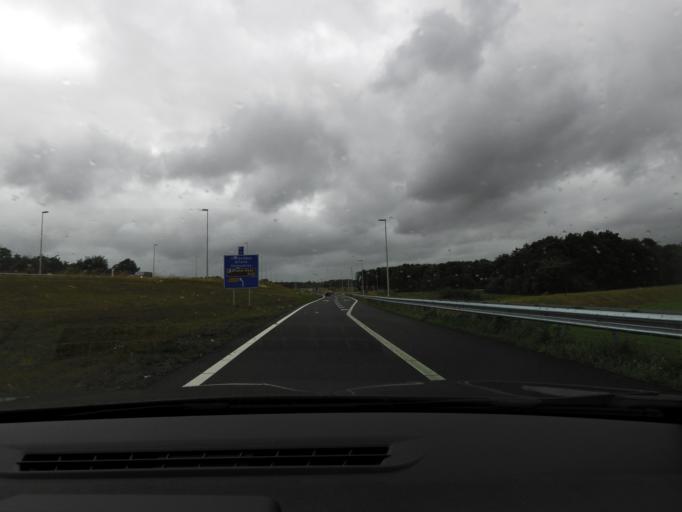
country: NL
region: South Holland
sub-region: Gemeente Brielle
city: Brielle
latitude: 51.8885
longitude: 4.1958
